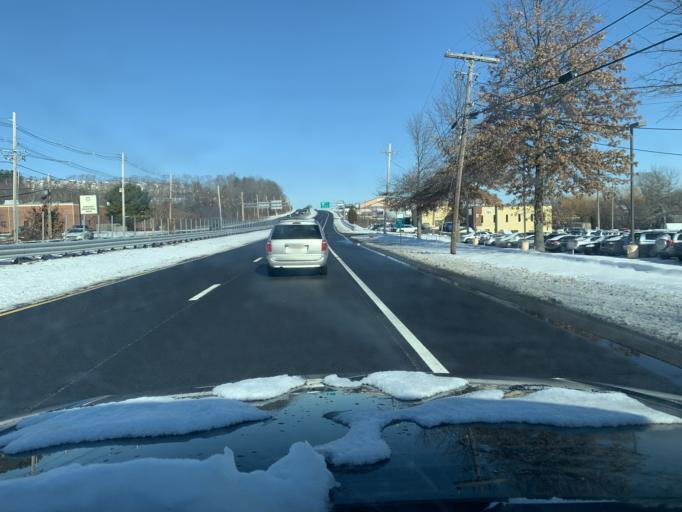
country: US
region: Massachusetts
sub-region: Essex County
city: Danvers
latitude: 42.5736
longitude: -70.9716
